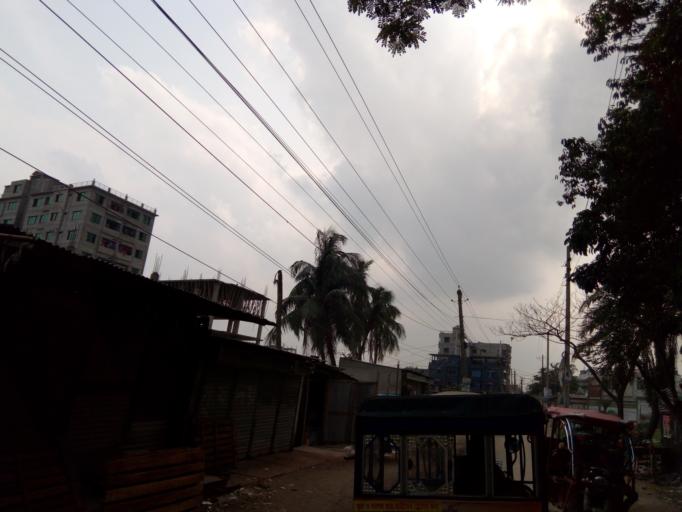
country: BD
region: Dhaka
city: Paltan
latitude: 23.7106
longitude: 90.4857
